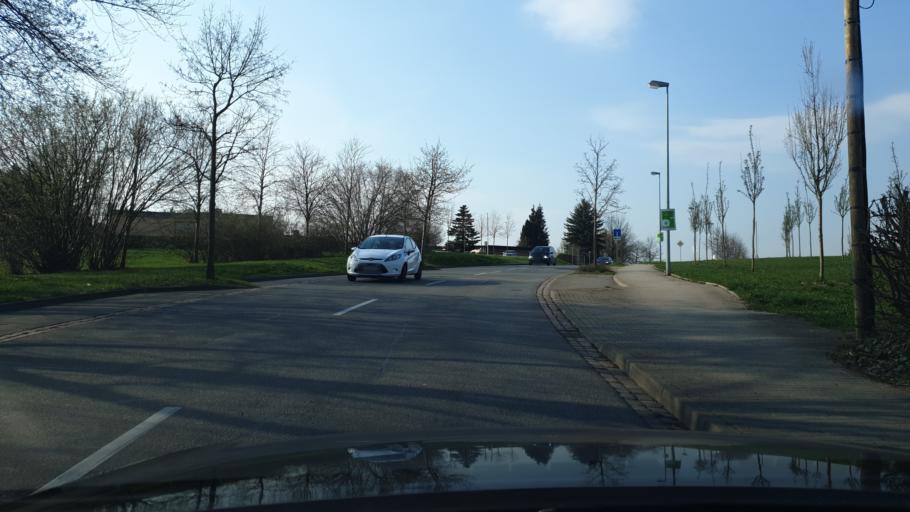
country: DE
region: Saxony
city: Mittweida
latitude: 50.9805
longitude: 12.9715
